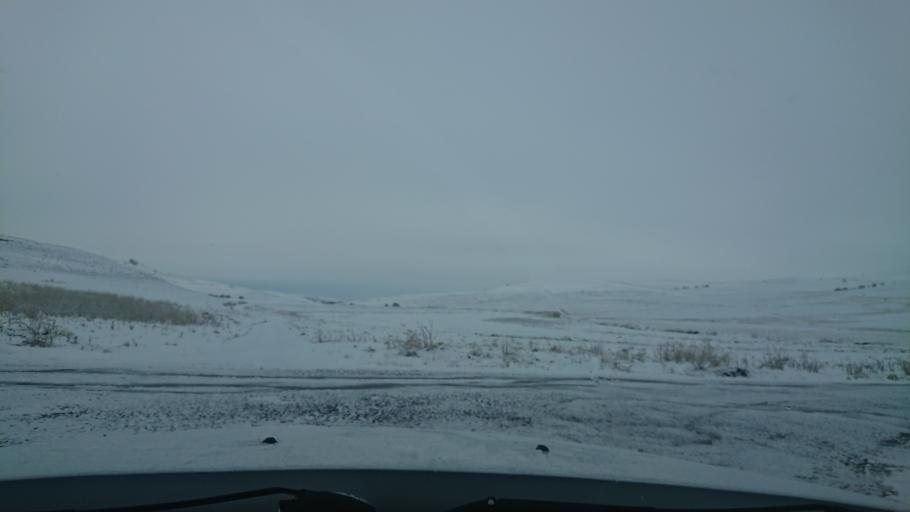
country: TR
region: Aksaray
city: Acipinar
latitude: 38.6825
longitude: 33.8628
